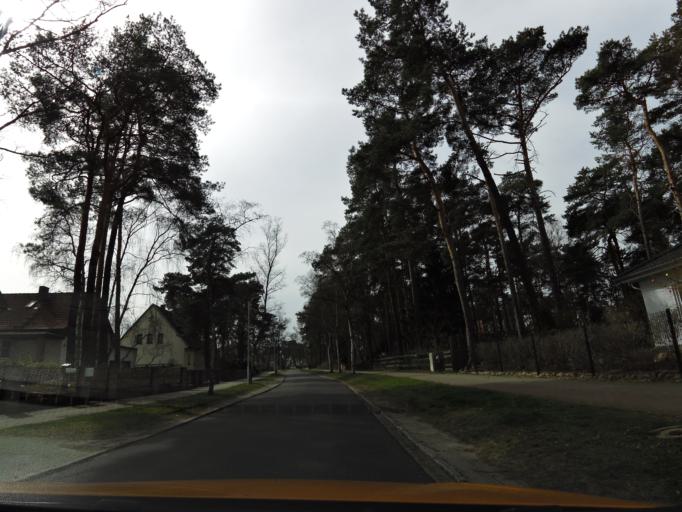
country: DE
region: Brandenburg
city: Rangsdorf
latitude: 52.3404
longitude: 13.4227
